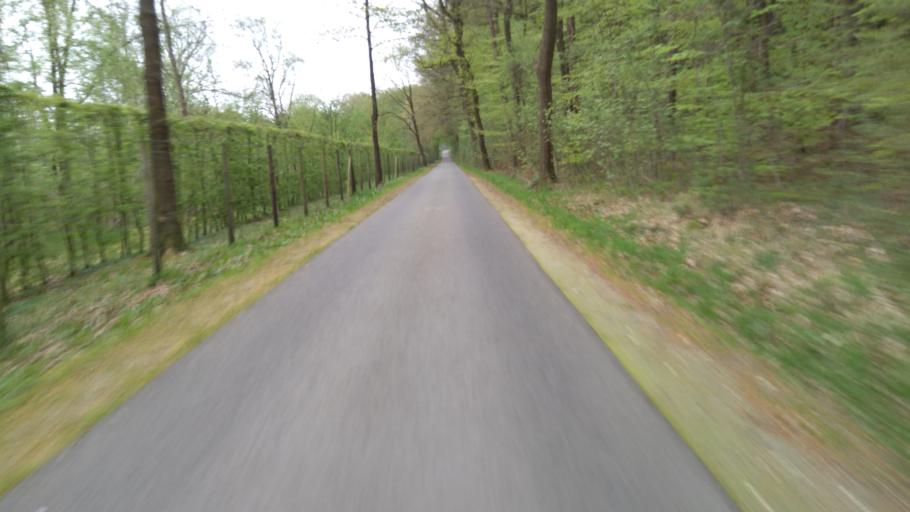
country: DE
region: Lower Saxony
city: Bliedersdorf
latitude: 53.4557
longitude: 9.5413
